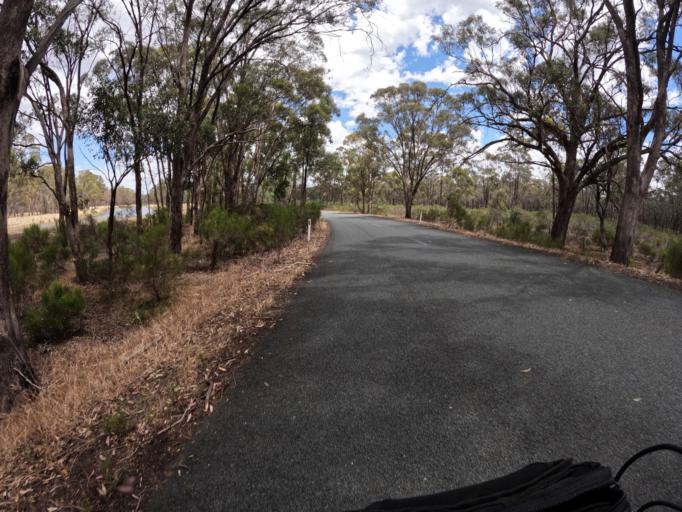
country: AU
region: Victoria
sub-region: Greater Shepparton
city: Shepparton
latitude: -36.6851
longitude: 145.1816
